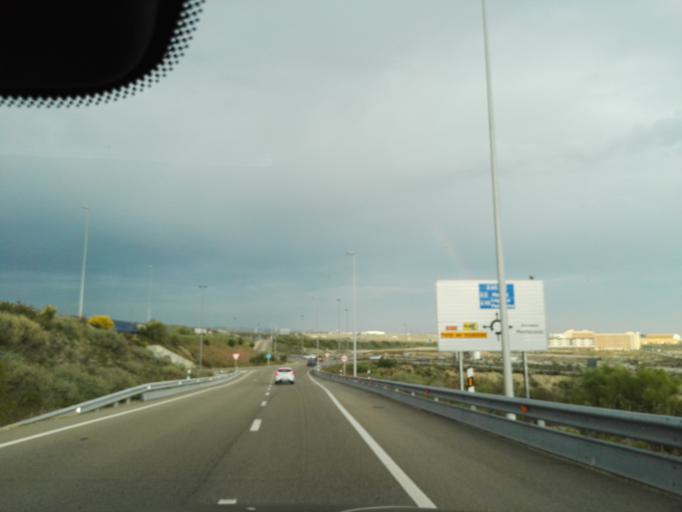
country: ES
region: Aragon
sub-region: Provincia de Zaragoza
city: Montecanal
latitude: 41.6191
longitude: -0.9589
